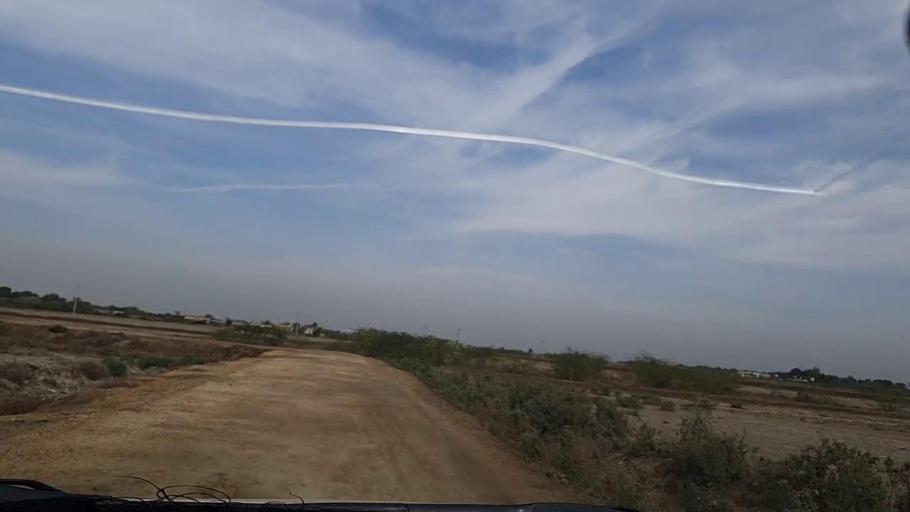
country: PK
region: Sindh
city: Dhoro Naro
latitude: 25.4500
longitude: 69.4897
